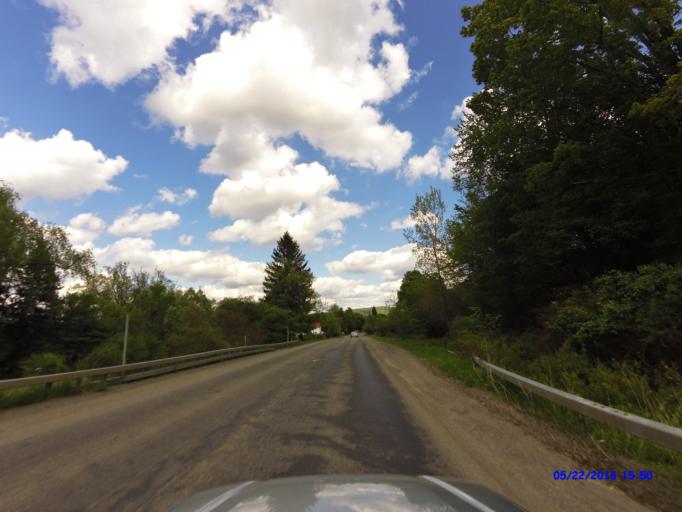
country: US
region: New York
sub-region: Cattaraugus County
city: Franklinville
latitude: 42.3376
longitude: -78.4730
